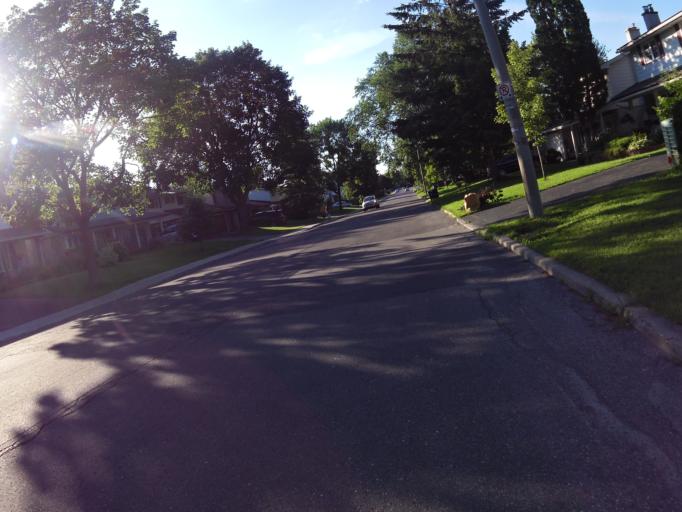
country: CA
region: Ontario
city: Bells Corners
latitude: 45.3407
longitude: -75.7956
